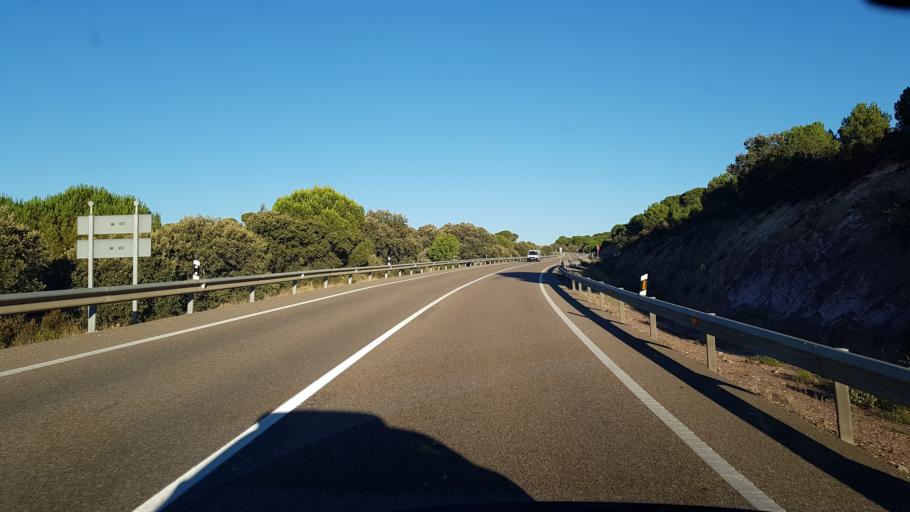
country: ES
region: Castille and Leon
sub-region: Provincia de Zamora
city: Palacios del Pan
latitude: 41.5383
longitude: -5.8450
